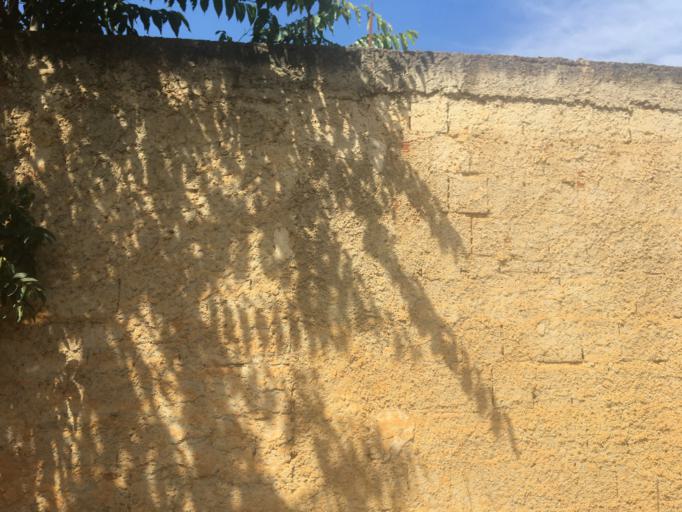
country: BR
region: Federal District
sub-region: Brasilia
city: Brasilia
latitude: -15.9656
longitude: -48.1314
